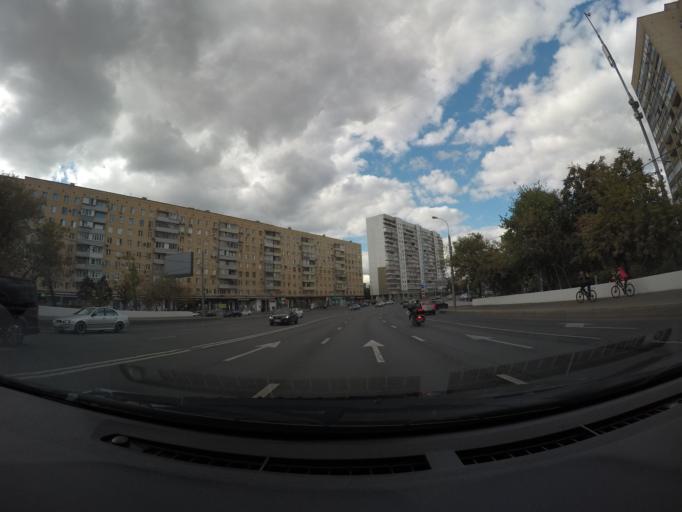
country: RU
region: Moscow
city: Mar'ina Roshcha
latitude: 55.7943
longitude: 37.5853
